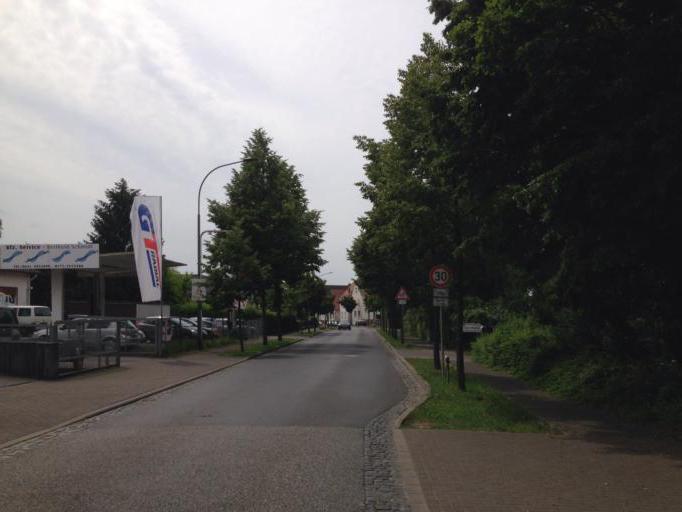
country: DE
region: Hesse
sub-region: Regierungsbezirk Giessen
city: Alten Buseck
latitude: 50.6027
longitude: 8.7548
